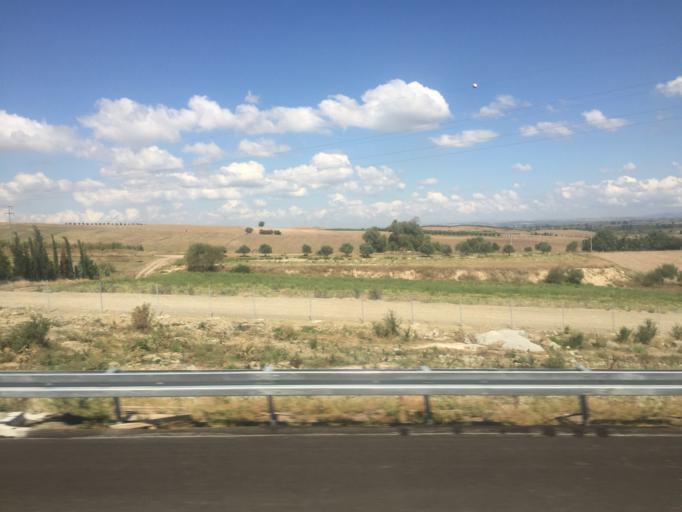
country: TR
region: Balikesir
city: Gobel
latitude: 40.0476
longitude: 28.2274
